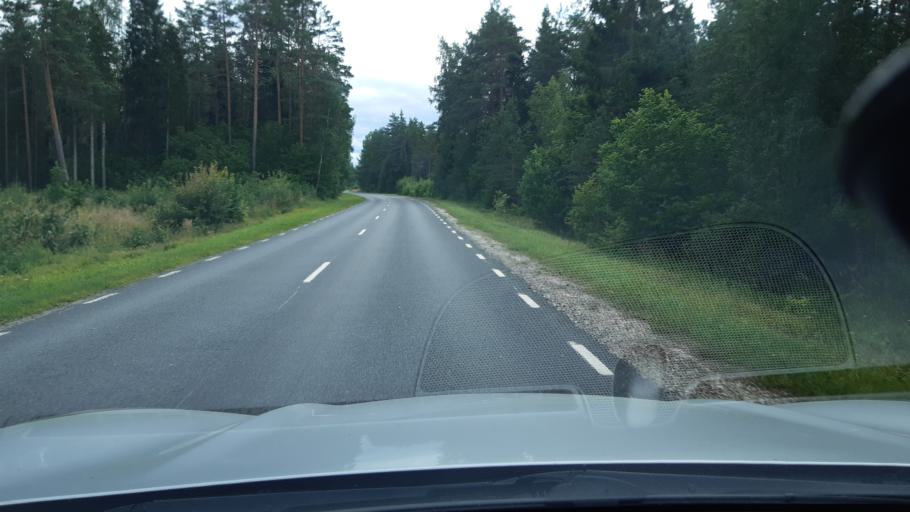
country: EE
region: Raplamaa
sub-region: Maerjamaa vald
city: Marjamaa
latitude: 59.0289
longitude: 24.5540
